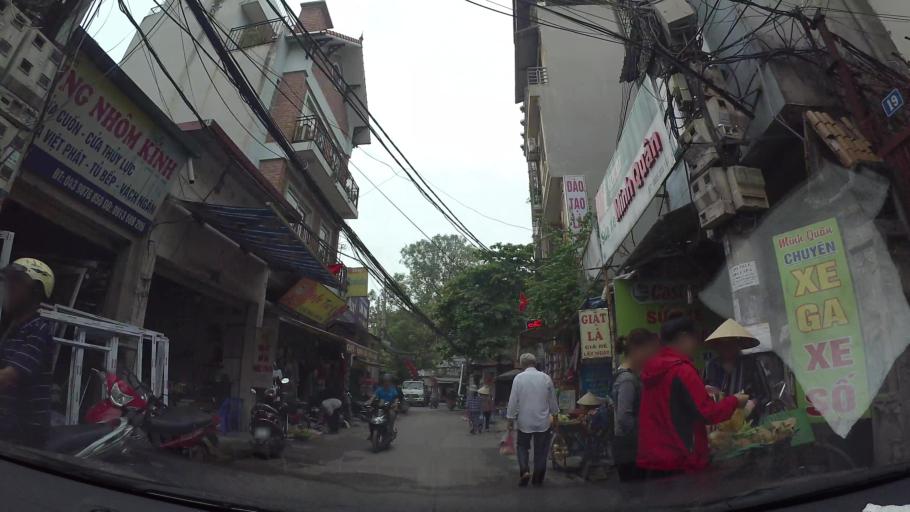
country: VN
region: Ha Noi
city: Hai BaTrung
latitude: 20.9872
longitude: 105.8885
